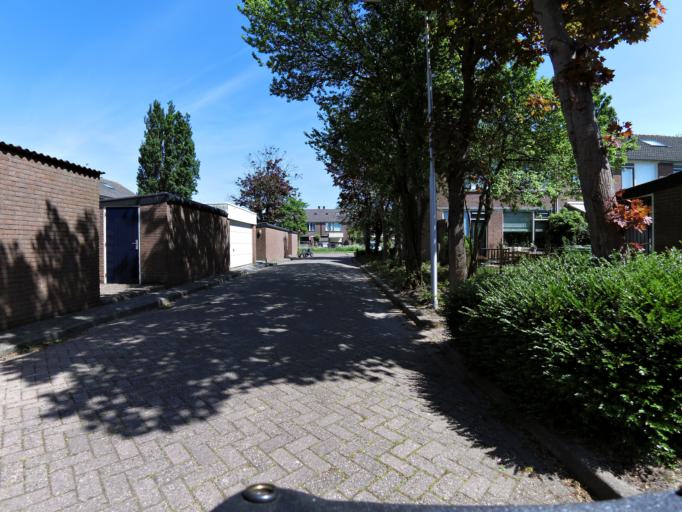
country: NL
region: South Holland
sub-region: Gemeente Binnenmaas
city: Heinenoord
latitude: 51.8283
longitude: 4.4818
